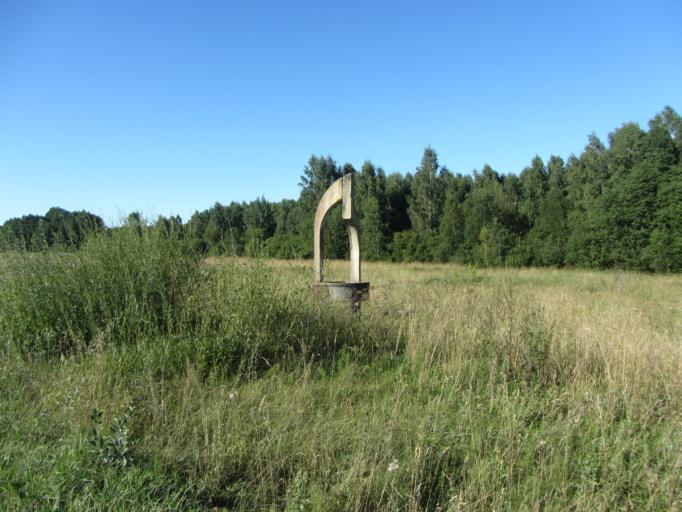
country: LT
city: Obeliai
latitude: 55.7851
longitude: 25.2619
